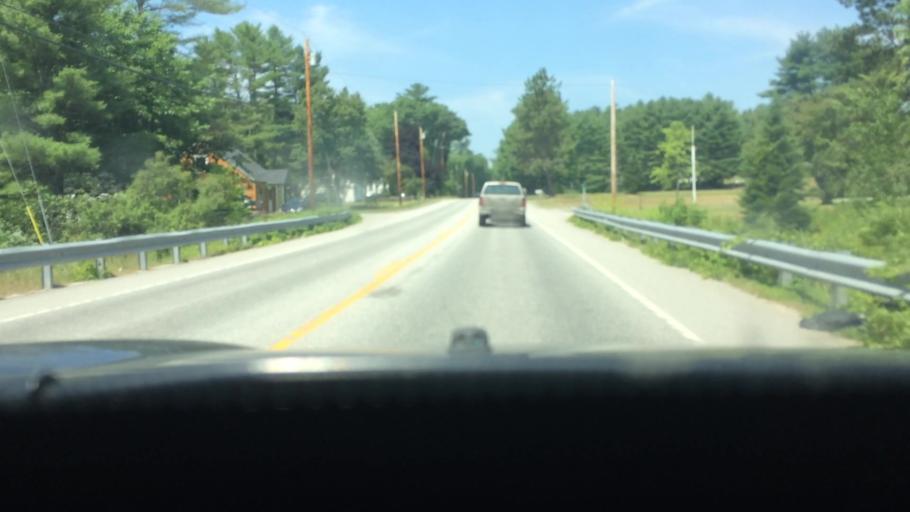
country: US
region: Maine
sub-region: Androscoggin County
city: Minot
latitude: 44.0817
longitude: -70.3083
